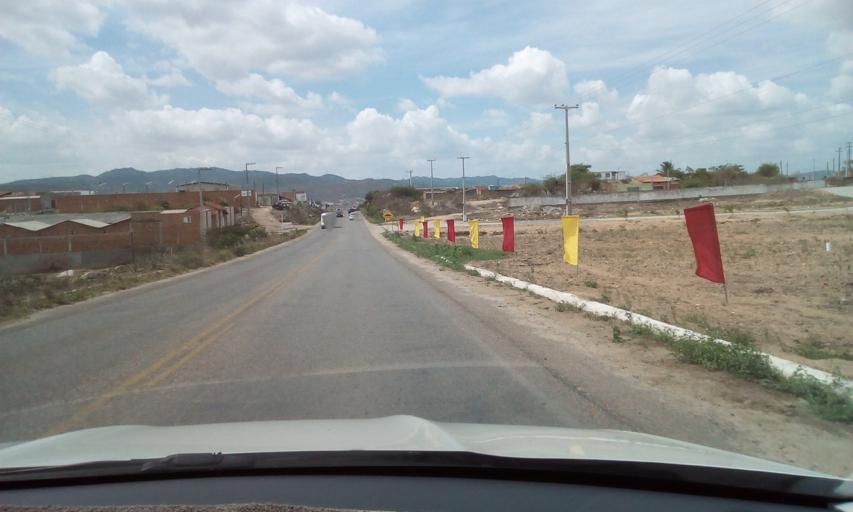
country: BR
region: Pernambuco
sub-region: Bezerros
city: Bezerros
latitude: -8.2571
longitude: -35.7573
